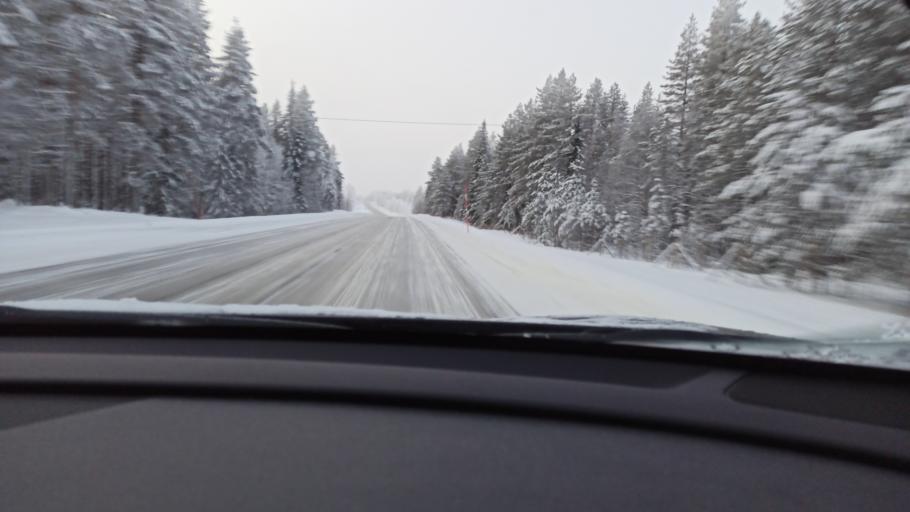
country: FI
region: Lapland
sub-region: Pohjois-Lappi
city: Sodankylae
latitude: 66.9951
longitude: 26.3591
